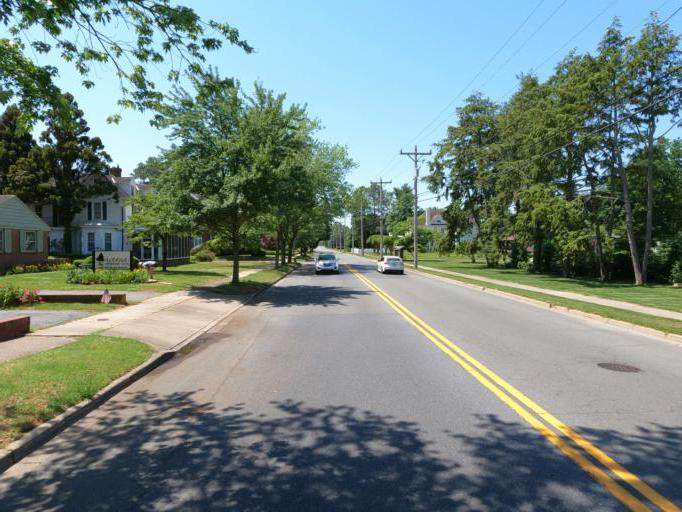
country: US
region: Delaware
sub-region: Sussex County
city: Milford
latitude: 38.9090
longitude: -75.4342
